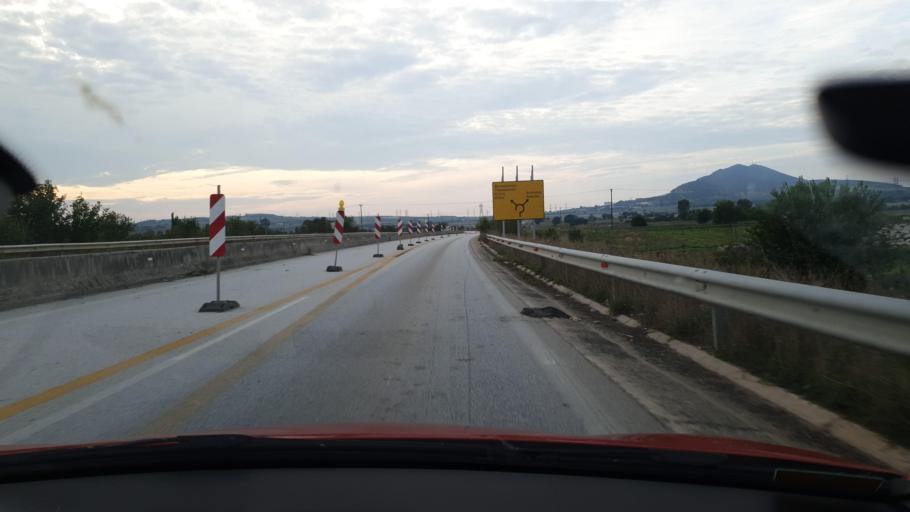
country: GR
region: Central Macedonia
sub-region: Nomos Thessalonikis
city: Assiros
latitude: 40.7845
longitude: 23.0125
